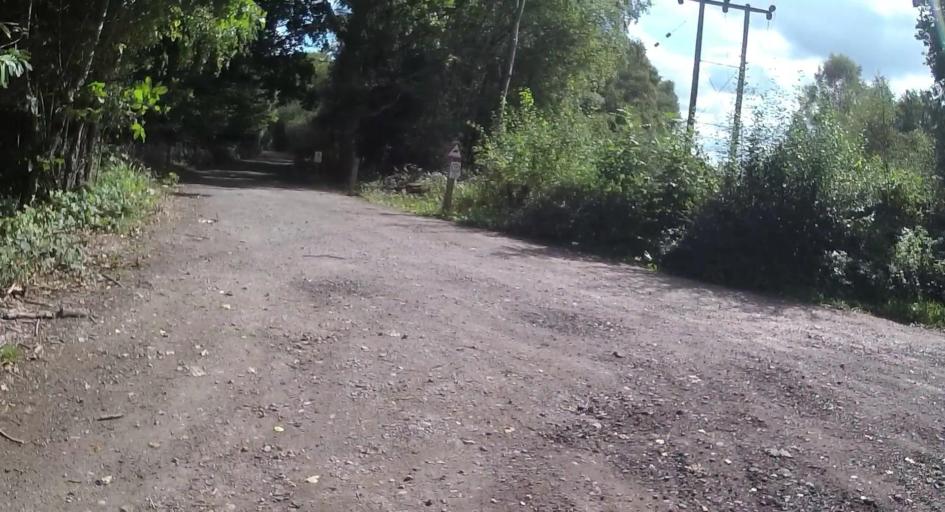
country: GB
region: England
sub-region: Surrey
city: Chobham
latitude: 51.3666
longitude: -0.6078
